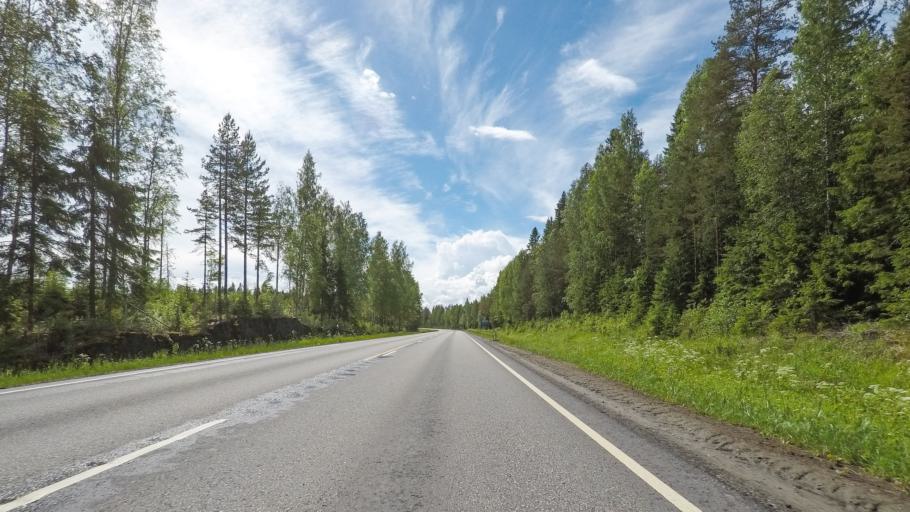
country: FI
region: Central Finland
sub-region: Jyvaeskylae
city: Hankasalmi
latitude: 62.3683
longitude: 26.5794
